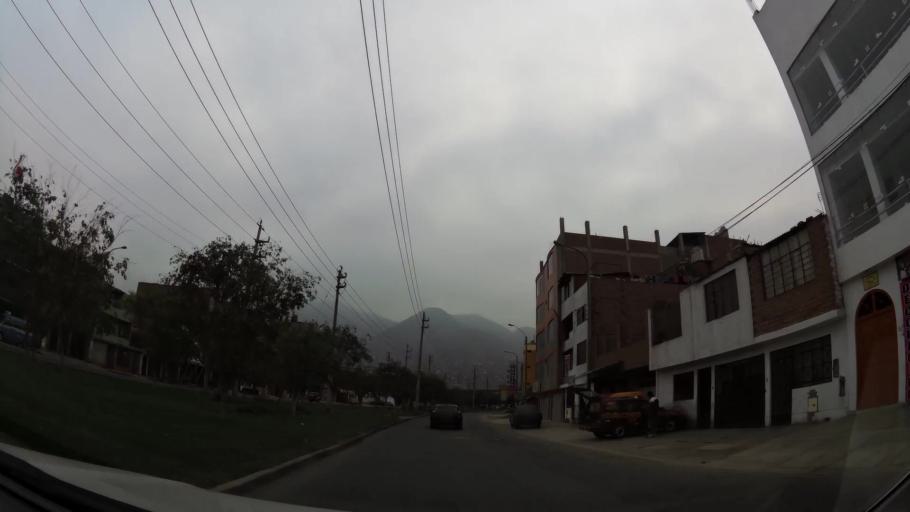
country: PE
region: Lima
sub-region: Lima
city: Independencia
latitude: -11.9900
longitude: -77.0089
